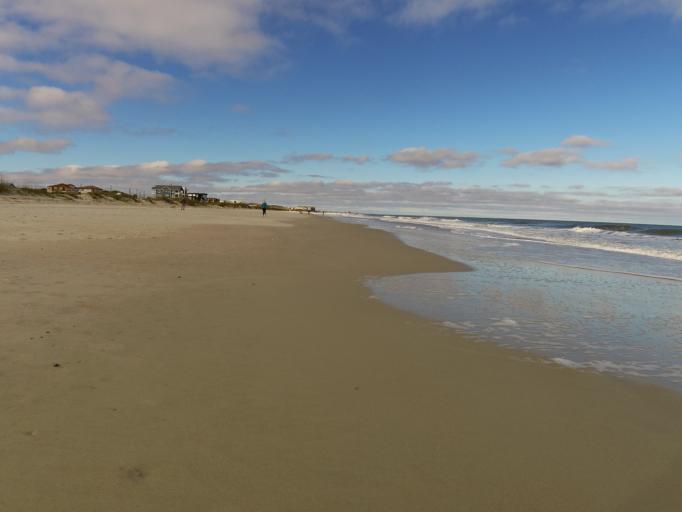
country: US
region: Florida
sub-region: Nassau County
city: Fernandina Beach
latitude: 30.5670
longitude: -81.4428
